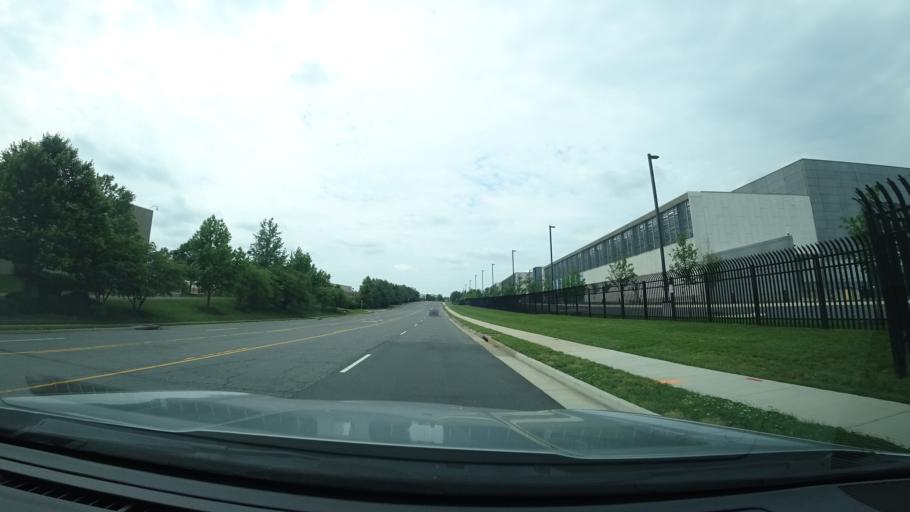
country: US
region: Virginia
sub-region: Loudoun County
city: Dulles Town Center
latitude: 39.0271
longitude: -77.4133
